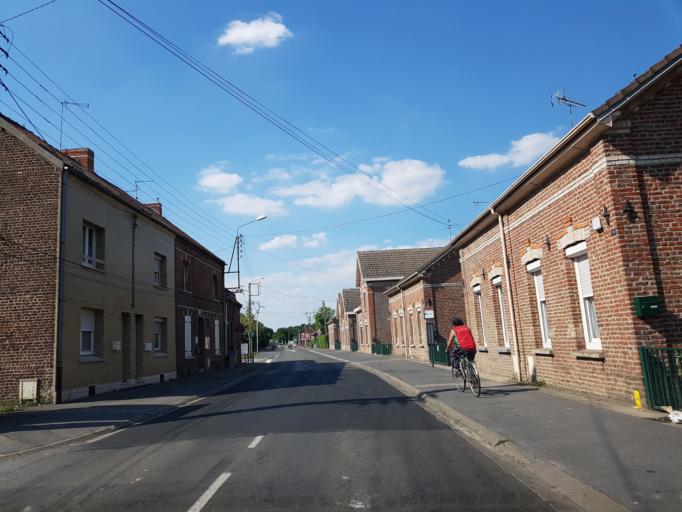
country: FR
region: Nord-Pas-de-Calais
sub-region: Departement du Nord
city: Lourches
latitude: 50.3200
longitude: 3.3429
